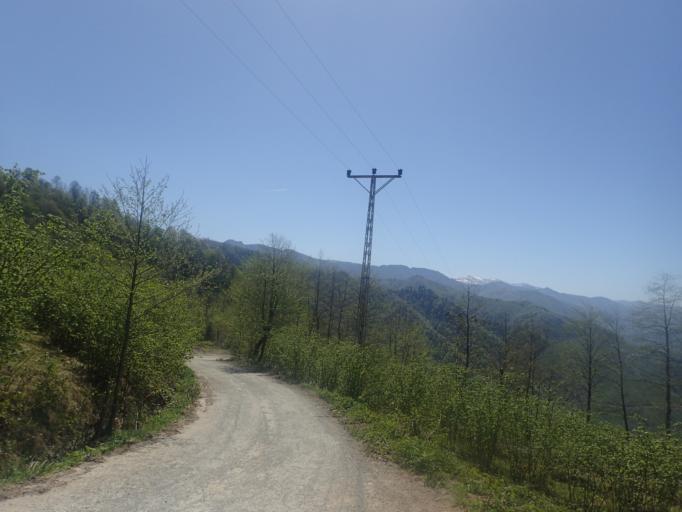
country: TR
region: Ordu
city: Kabaduz
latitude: 40.8016
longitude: 37.9079
